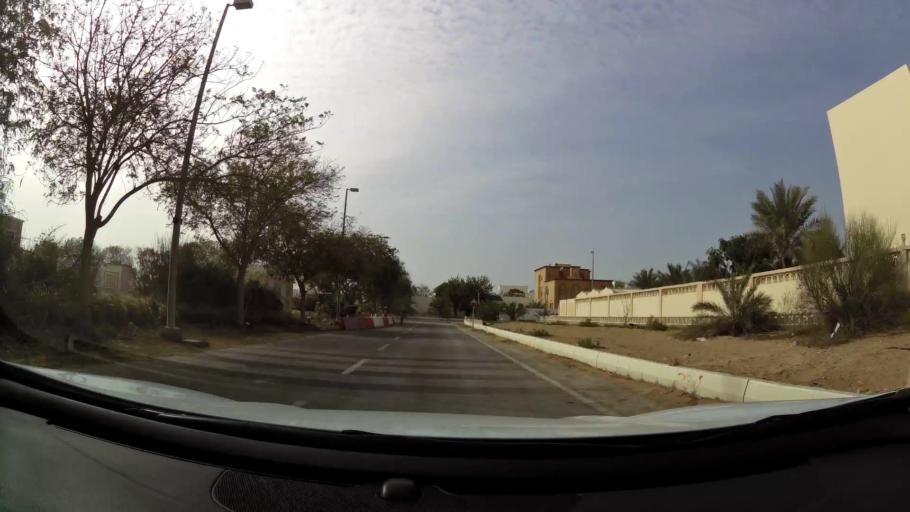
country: AE
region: Abu Dhabi
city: Abu Dhabi
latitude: 24.6016
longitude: 54.7025
